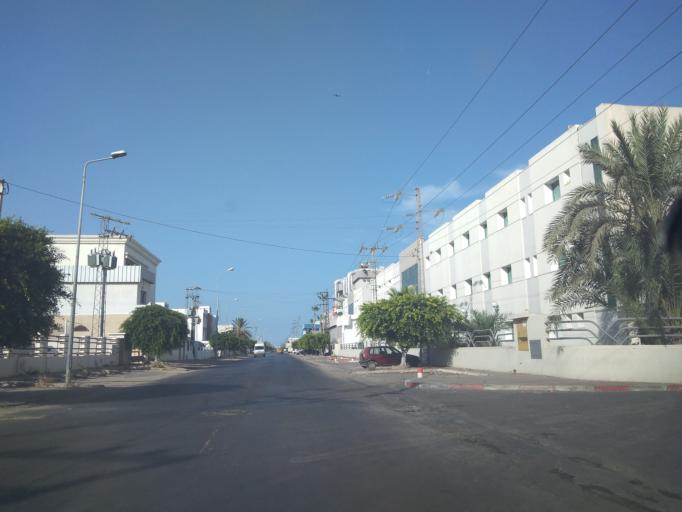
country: TN
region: Safaqis
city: Sfax
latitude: 34.7462
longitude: 10.7700
